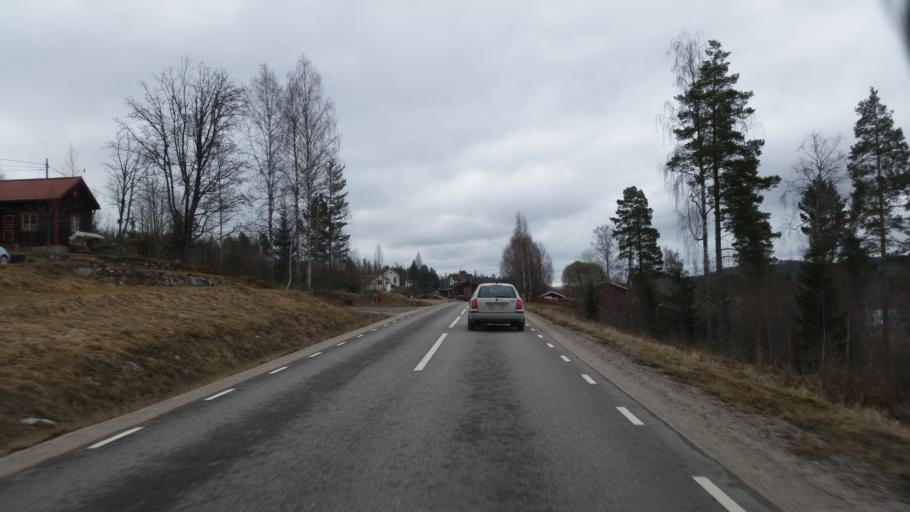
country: SE
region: Gaevleborg
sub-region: Ovanakers Kommun
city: Edsbyn
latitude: 61.4132
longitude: 15.7602
